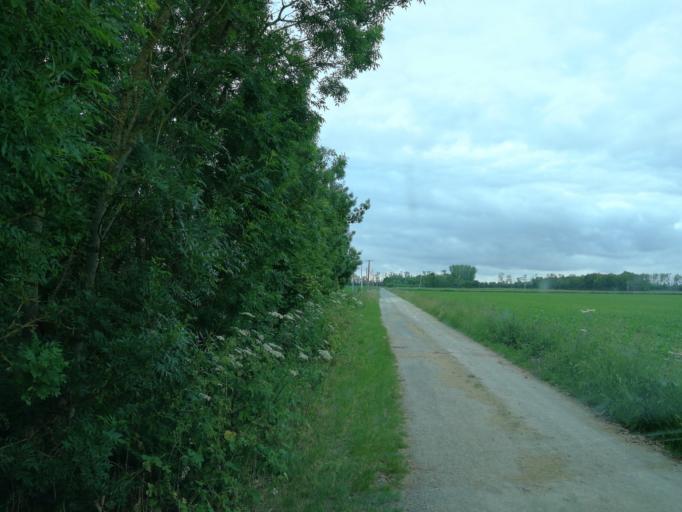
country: FR
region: Poitou-Charentes
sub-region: Departement de la Charente-Maritime
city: Marans
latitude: 46.3628
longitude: -0.9538
